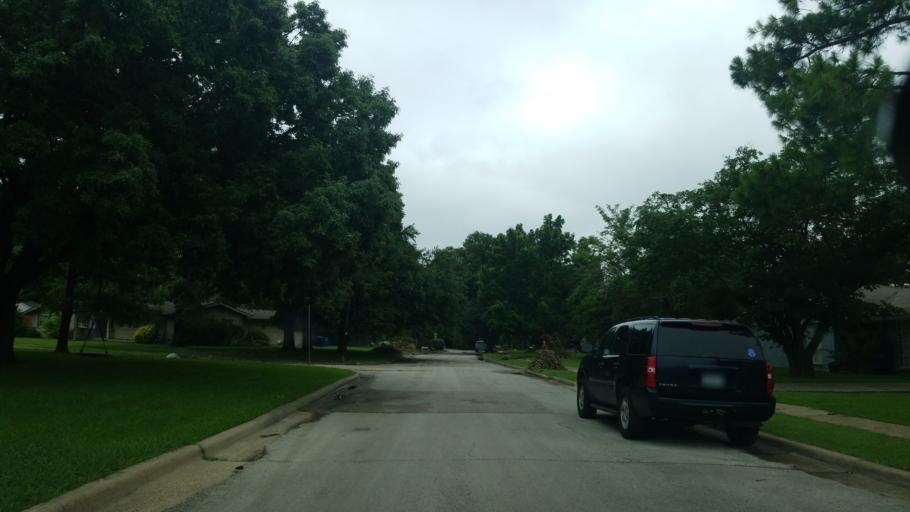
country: US
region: Texas
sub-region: Dallas County
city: Farmers Branch
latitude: 32.8982
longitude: -96.8706
